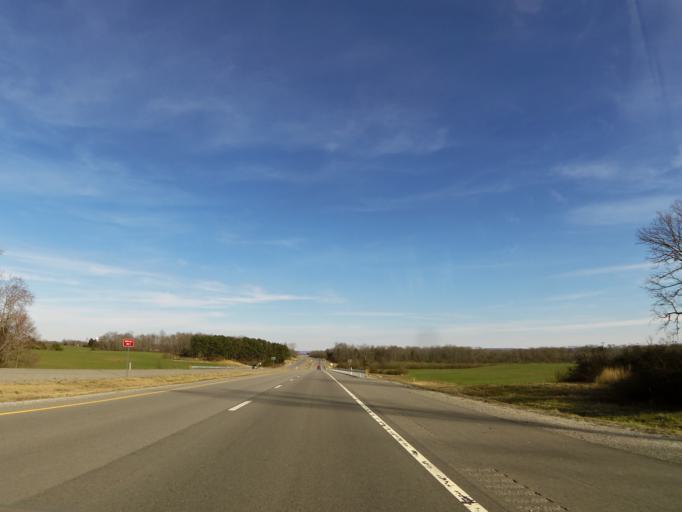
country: US
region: Tennessee
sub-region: Warren County
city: McMinnville
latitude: 35.7225
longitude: -85.8827
